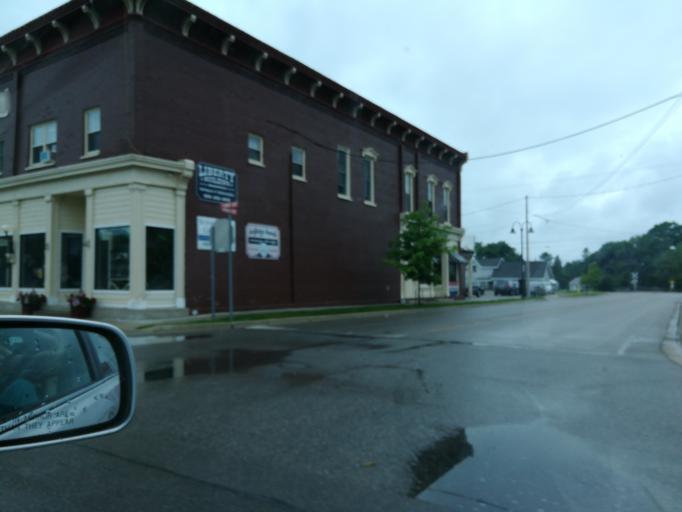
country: US
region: Michigan
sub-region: Iosco County
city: Tawas City
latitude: 44.2698
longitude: -83.5148
